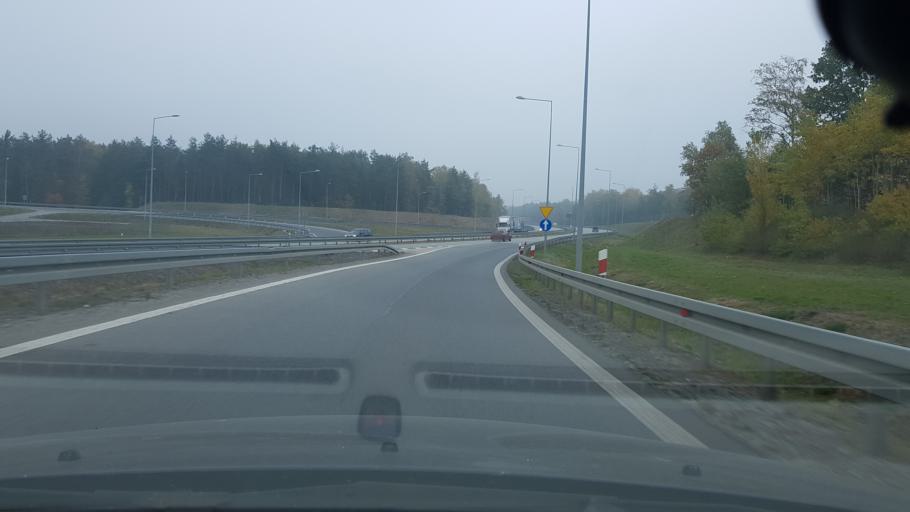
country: PL
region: Lodz Voivodeship
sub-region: Powiat tomaszowski
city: Tomaszow Mazowiecki
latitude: 51.5650
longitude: 20.0221
